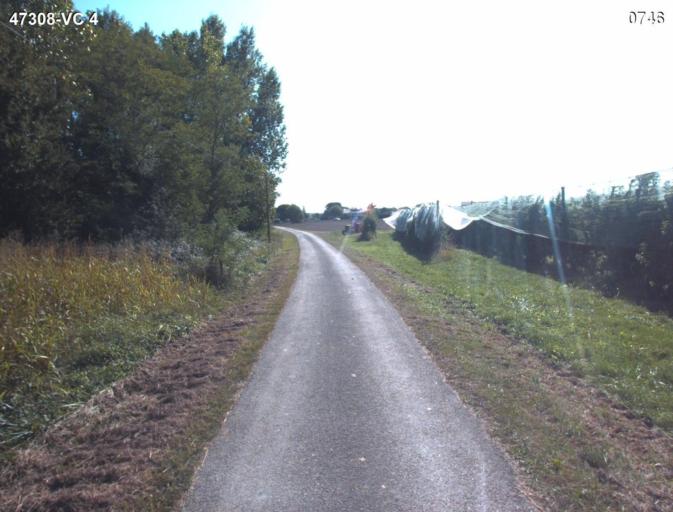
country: FR
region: Aquitaine
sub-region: Departement du Lot-et-Garonne
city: Buzet-sur-Baise
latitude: 44.2614
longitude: 0.3318
